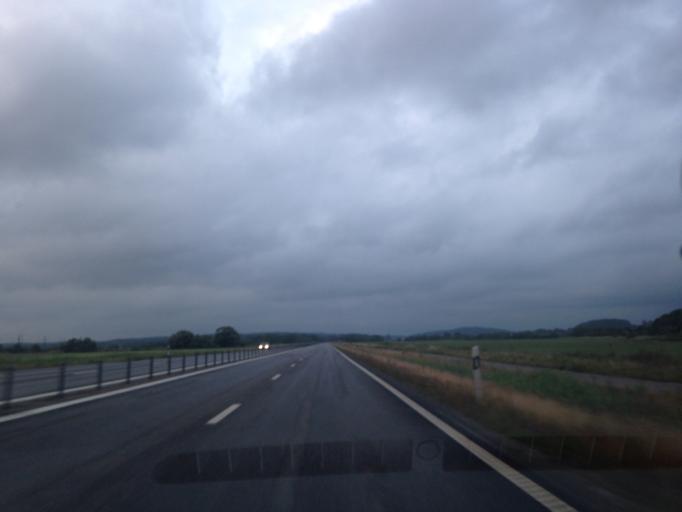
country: SE
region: Halland
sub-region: Varbergs Kommun
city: Varberg
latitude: 57.1309
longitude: 12.2617
